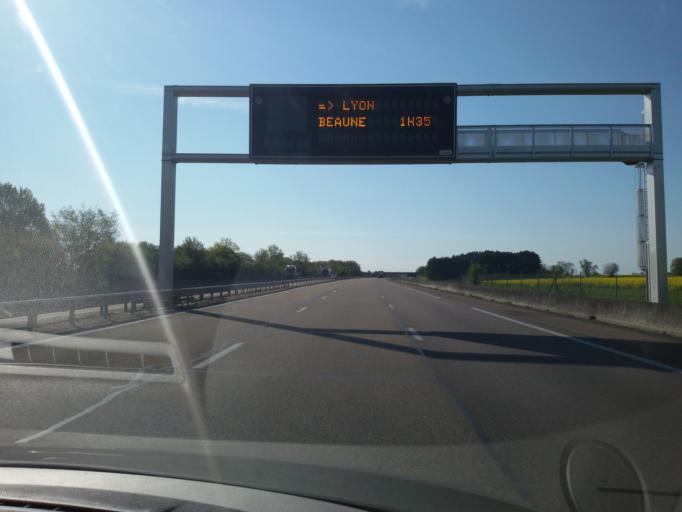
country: FR
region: Bourgogne
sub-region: Departement de l'Yonne
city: Saint-Julien-du-Sault
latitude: 47.9623
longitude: 3.2158
